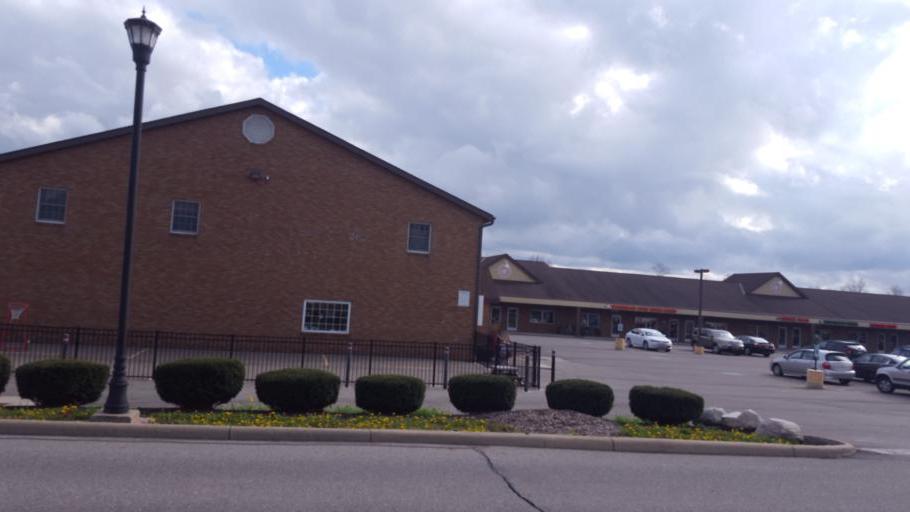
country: US
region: Ohio
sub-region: Delaware County
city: Powell
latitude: 40.1633
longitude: -83.0744
